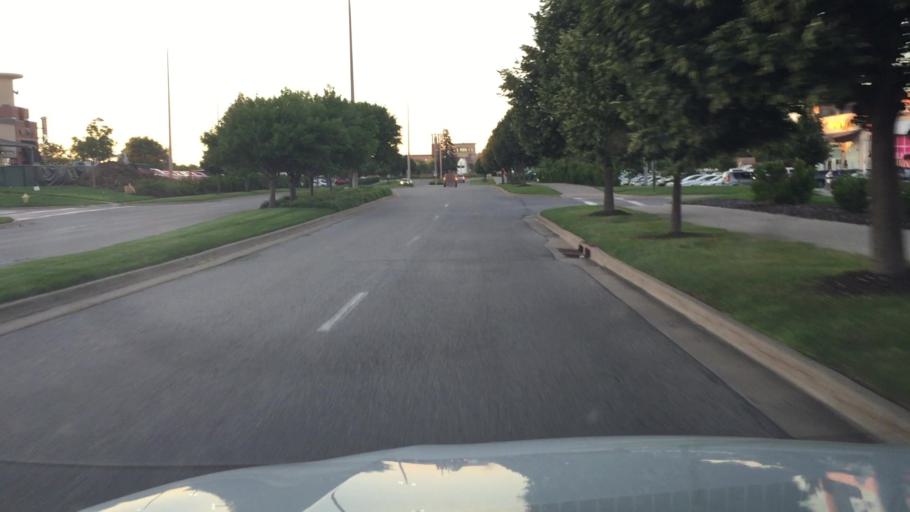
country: US
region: Iowa
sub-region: Polk County
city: Clive
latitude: 41.5639
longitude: -93.8038
